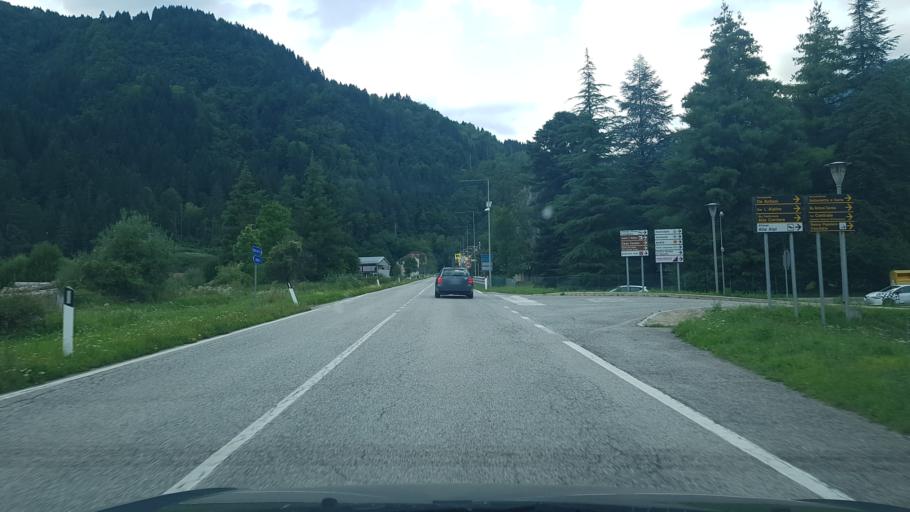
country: IT
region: Friuli Venezia Giulia
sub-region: Provincia di Udine
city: Comeglians
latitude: 46.5129
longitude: 12.8665
